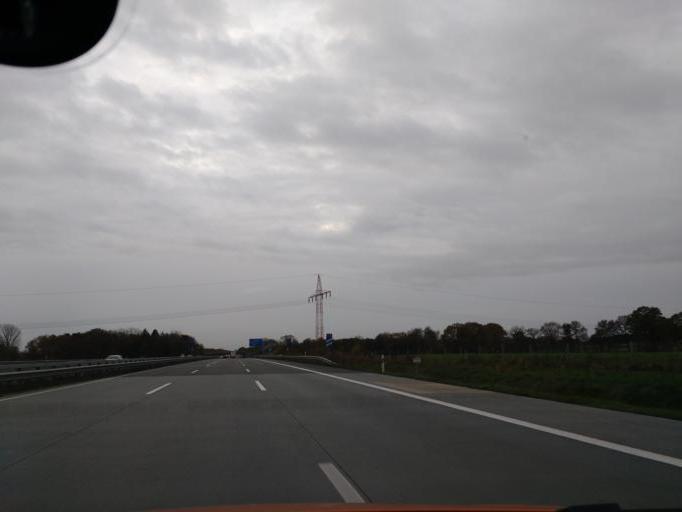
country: DE
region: Lower Saxony
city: Reessum
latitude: 53.1144
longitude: 9.2052
